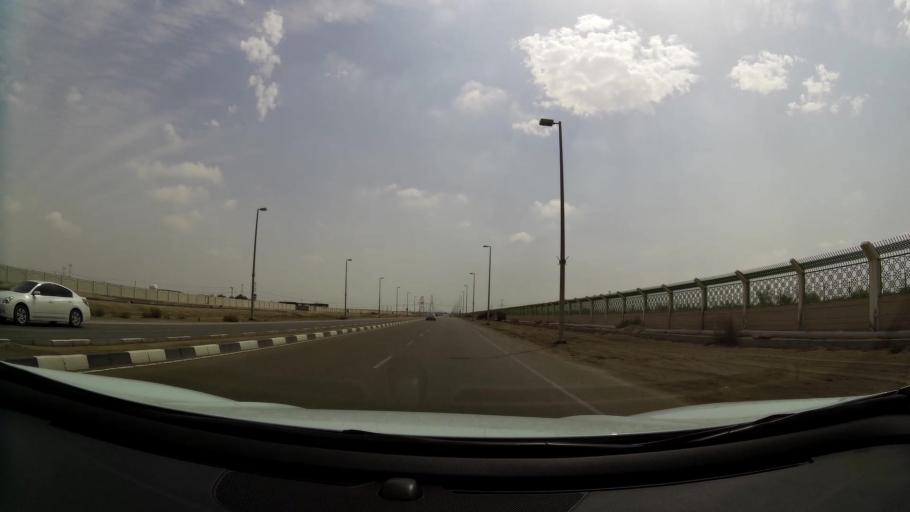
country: AE
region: Abu Dhabi
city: Abu Dhabi
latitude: 24.5317
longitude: 54.6368
